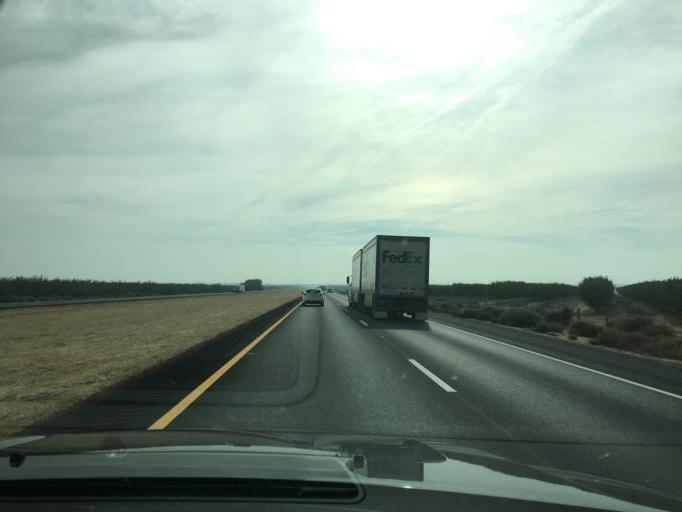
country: US
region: California
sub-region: Fresno County
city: Coalinga
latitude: 36.2793
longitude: -120.2599
